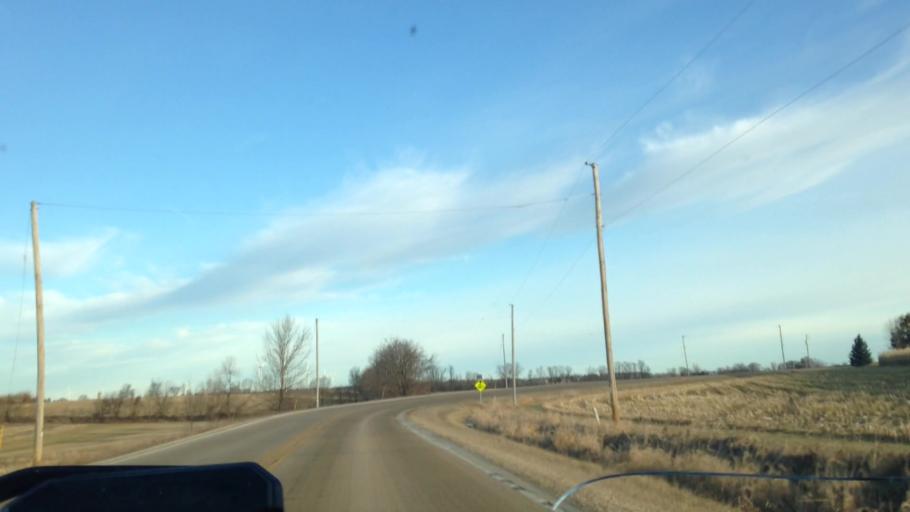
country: US
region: Wisconsin
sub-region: Dodge County
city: Mayville
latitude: 43.5190
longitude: -88.5153
